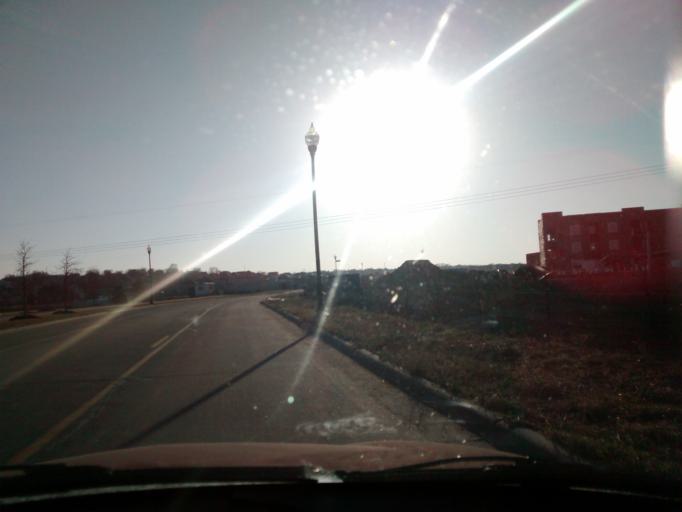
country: US
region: Nebraska
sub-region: Sarpy County
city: Offutt Air Force Base
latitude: 41.1470
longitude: -95.9750
